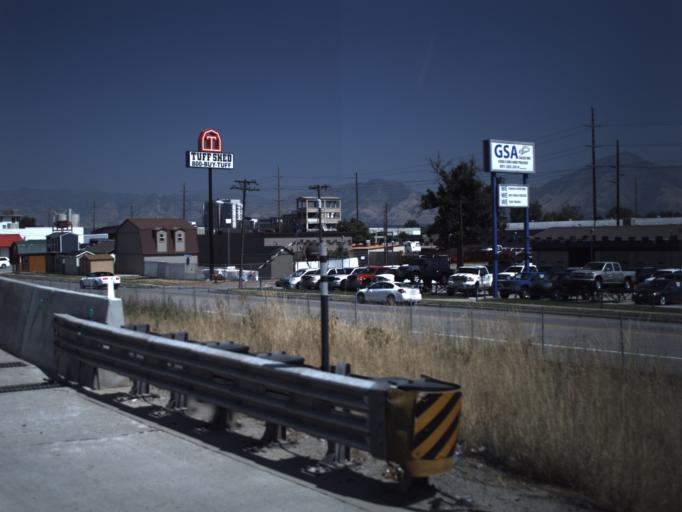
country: US
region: Utah
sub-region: Salt Lake County
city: Murray
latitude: 40.6496
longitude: -111.9018
